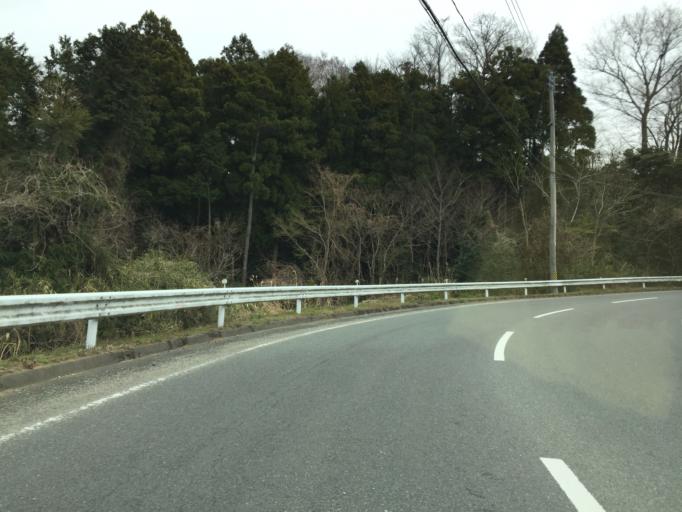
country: JP
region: Fukushima
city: Iwaki
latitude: 37.0451
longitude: 140.8864
